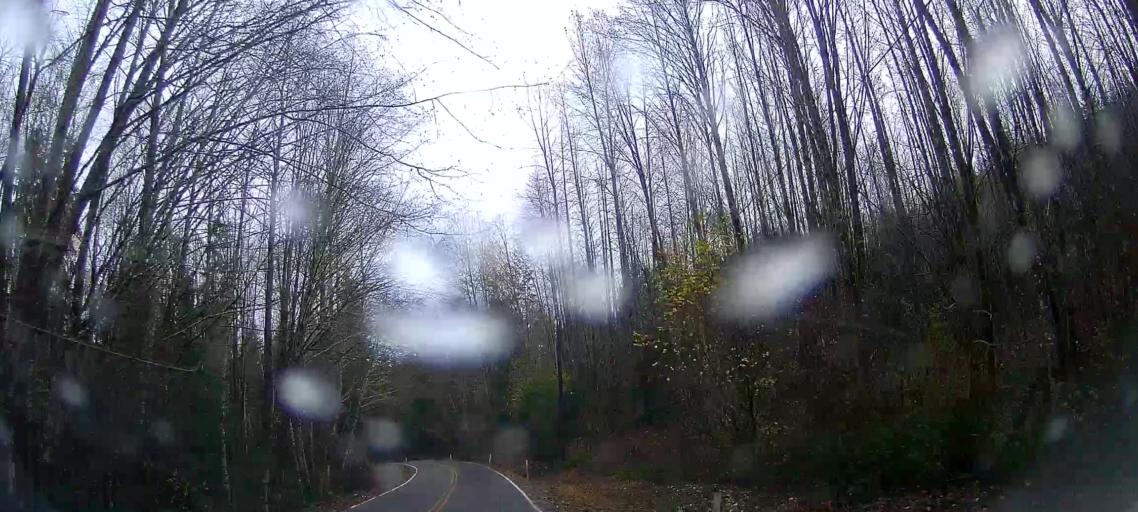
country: US
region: Washington
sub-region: Skagit County
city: Clear Lake
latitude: 48.4767
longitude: -122.1440
